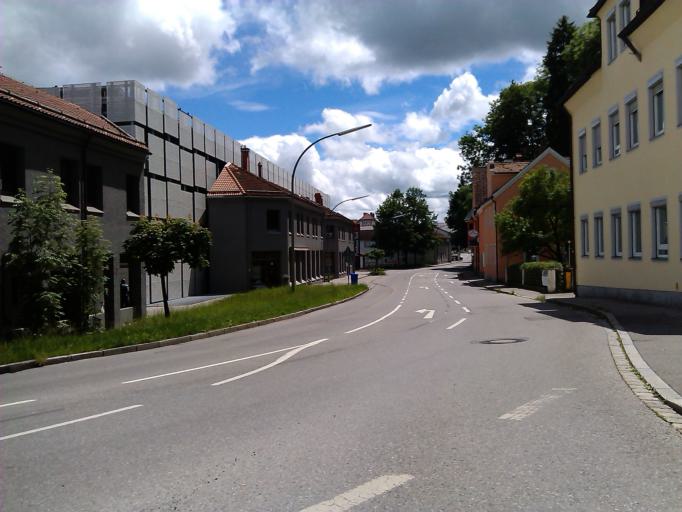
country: DE
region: Bavaria
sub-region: Swabia
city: Kaufbeuren
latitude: 47.8776
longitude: 10.6199
